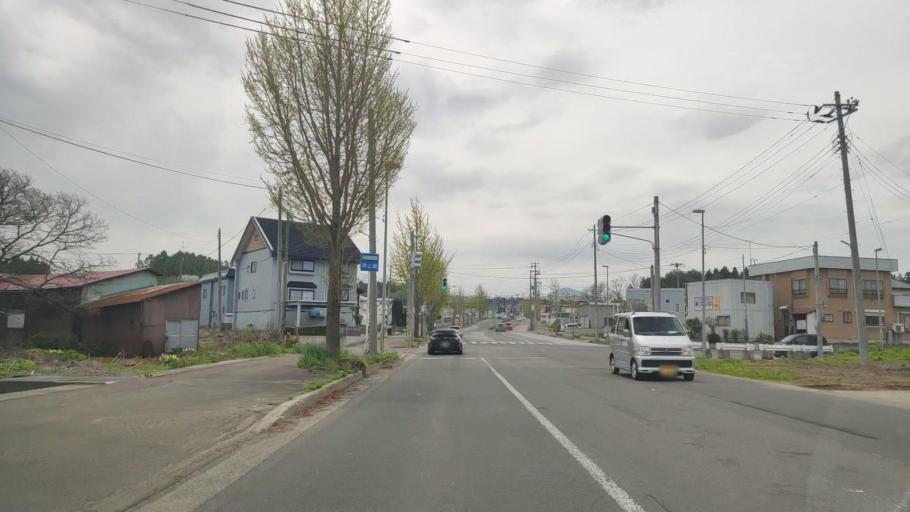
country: JP
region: Aomori
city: Aomori Shi
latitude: 40.7926
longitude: 140.7863
